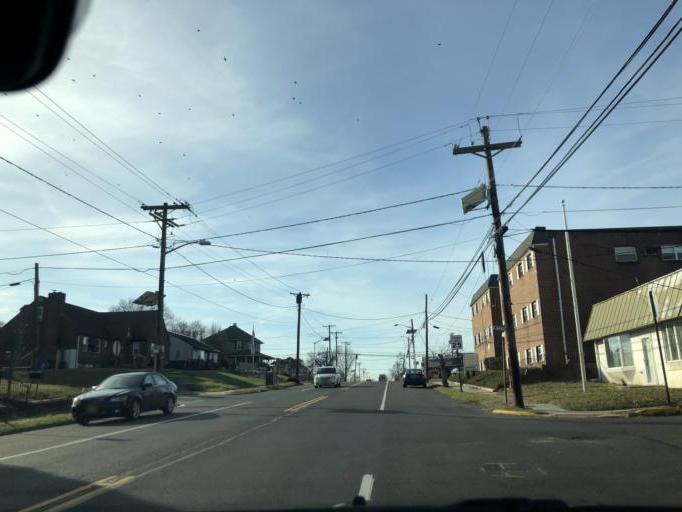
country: US
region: New Jersey
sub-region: Burlington County
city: Maple Shade
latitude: 39.9566
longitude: -74.9904
